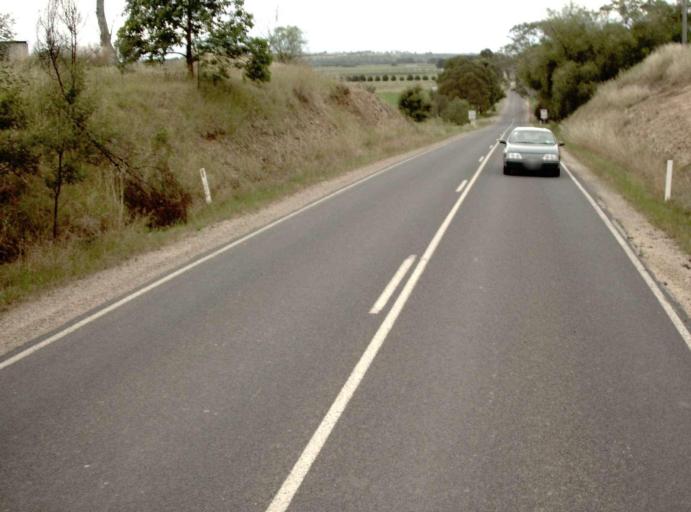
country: AU
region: Victoria
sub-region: East Gippsland
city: Bairnsdale
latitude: -37.8019
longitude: 147.4699
